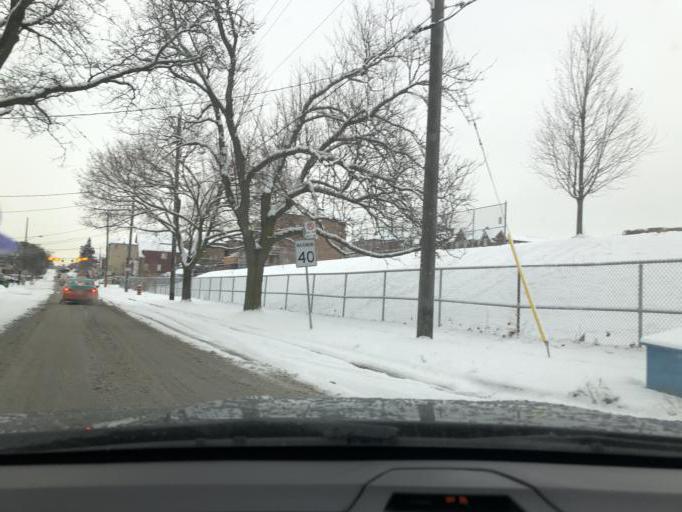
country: CA
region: Ontario
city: Toronto
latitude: 43.6863
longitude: -79.4708
